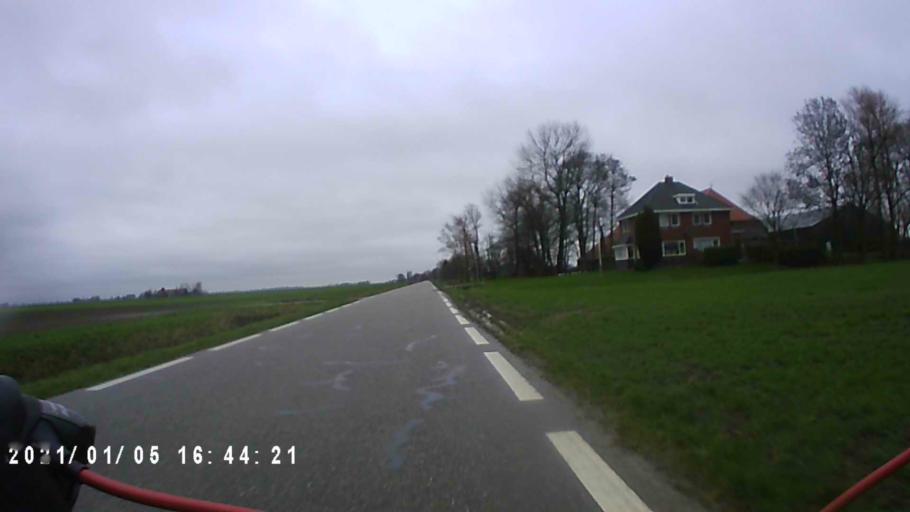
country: NL
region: Groningen
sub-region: Gemeente  Oldambt
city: Winschoten
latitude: 53.2175
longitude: 7.0518
